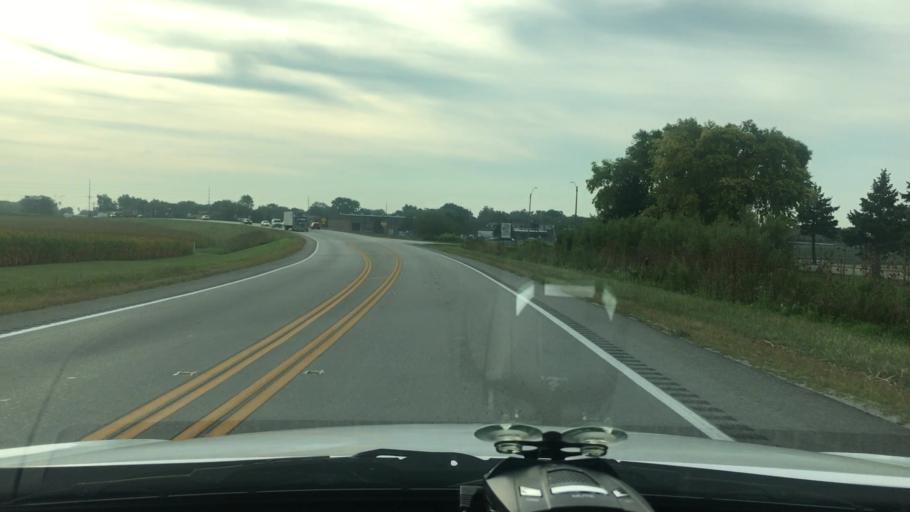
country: US
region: Illinois
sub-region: Champaign County
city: Champaign
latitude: 40.1400
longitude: -88.2829
